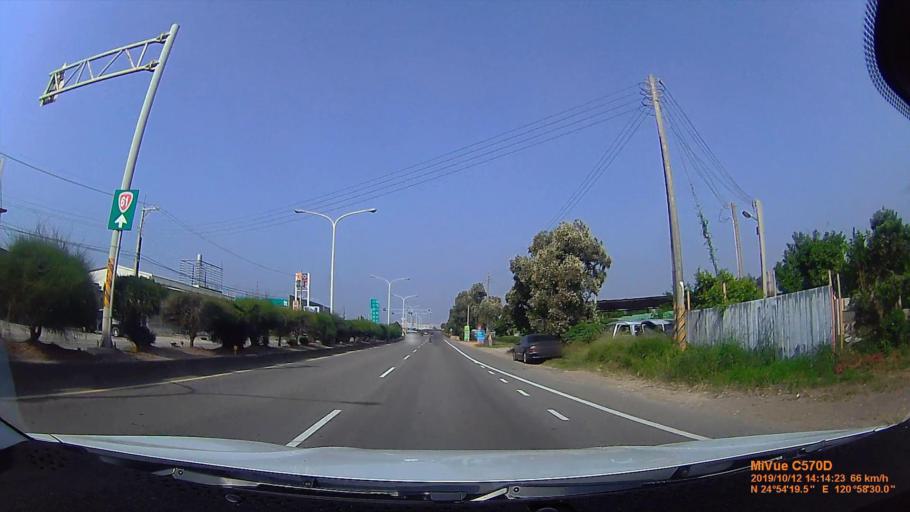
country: TW
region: Taiwan
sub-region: Hsinchu
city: Zhubei
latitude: 24.9094
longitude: 120.9781
